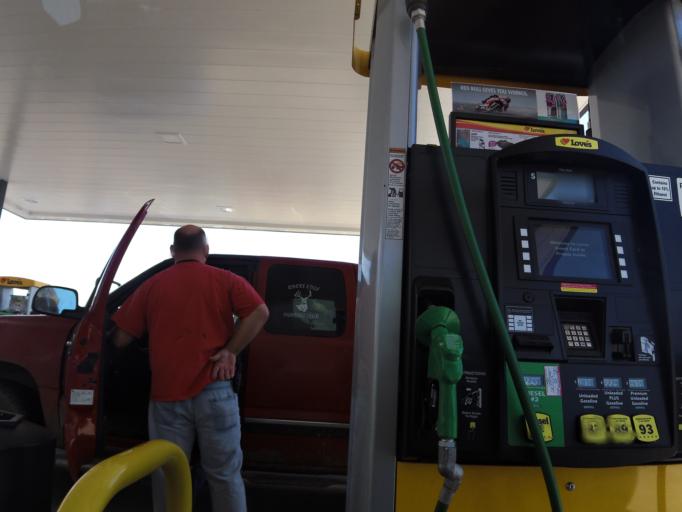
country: US
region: Tennessee
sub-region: Dyer County
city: Dyersburg
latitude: 36.0712
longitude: -89.3960
